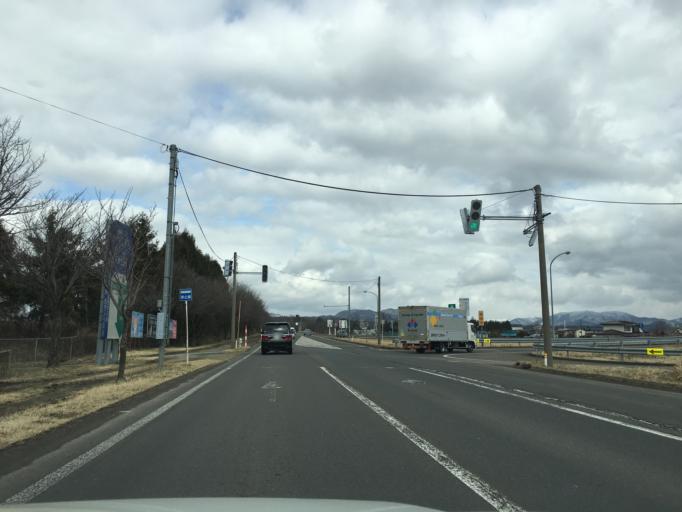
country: JP
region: Akita
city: Hanawa
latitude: 40.2564
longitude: 140.7614
